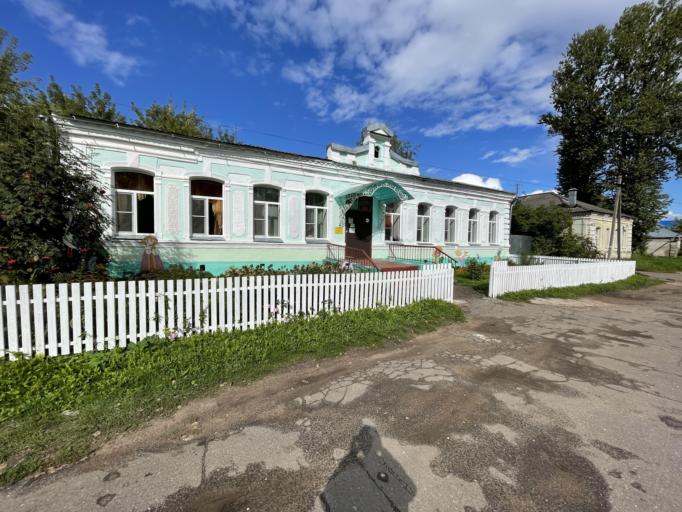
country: RU
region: Tverskaya
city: Vyshniy Volochek
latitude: 57.5788
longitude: 34.5590
